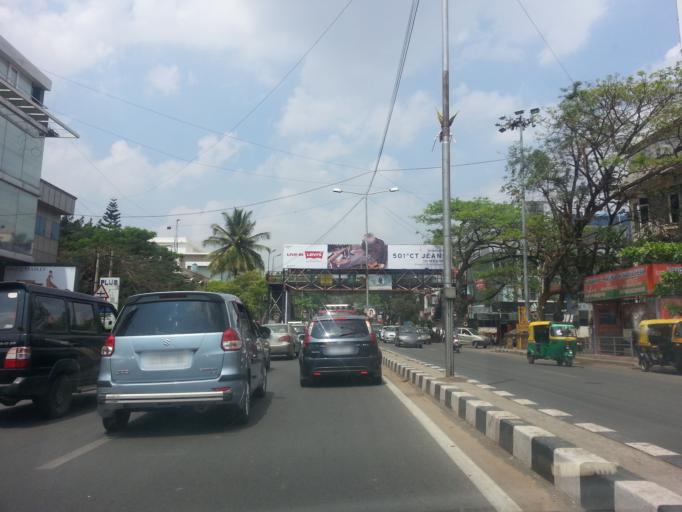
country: IN
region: Karnataka
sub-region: Bangalore Urban
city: Bangalore
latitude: 12.9629
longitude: 77.6416
